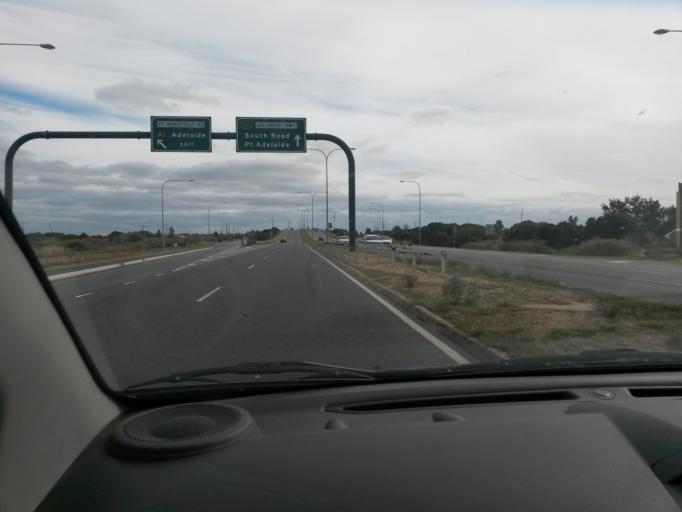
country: AU
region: South Australia
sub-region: Salisbury
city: Ingle Farm
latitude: -34.8080
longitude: 138.6007
